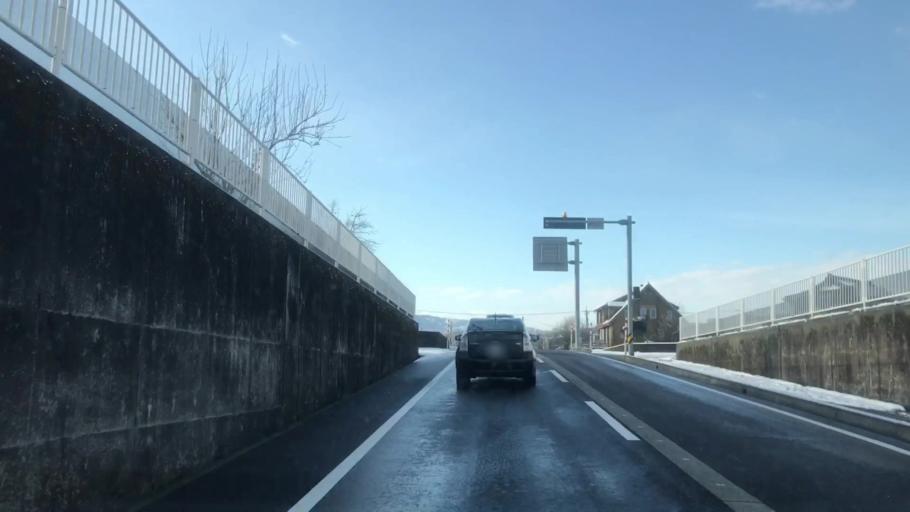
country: JP
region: Toyama
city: Toyama-shi
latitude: 36.6130
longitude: 137.2850
